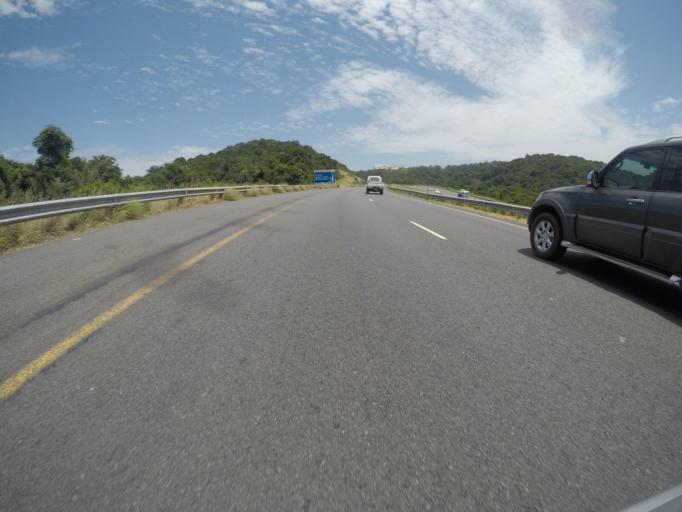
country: ZA
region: Eastern Cape
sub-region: Buffalo City Metropolitan Municipality
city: East London
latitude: -32.9702
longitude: 27.9103
